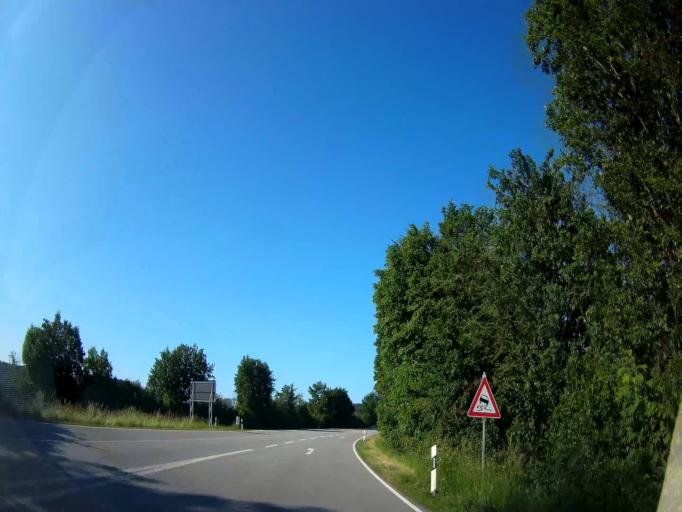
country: DE
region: Bavaria
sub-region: Upper Bavaria
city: Stammham
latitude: 48.2419
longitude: 12.9015
